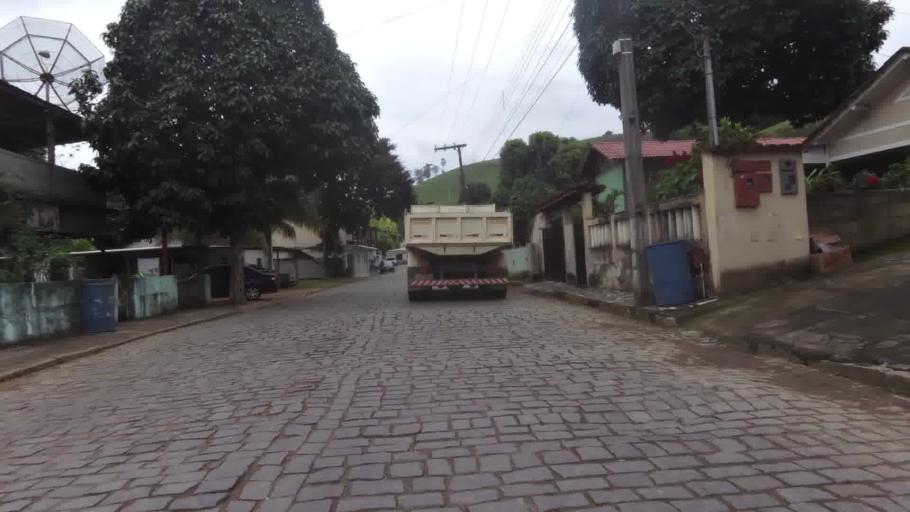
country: BR
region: Espirito Santo
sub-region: Iconha
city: Iconha
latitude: -20.7717
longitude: -40.8289
